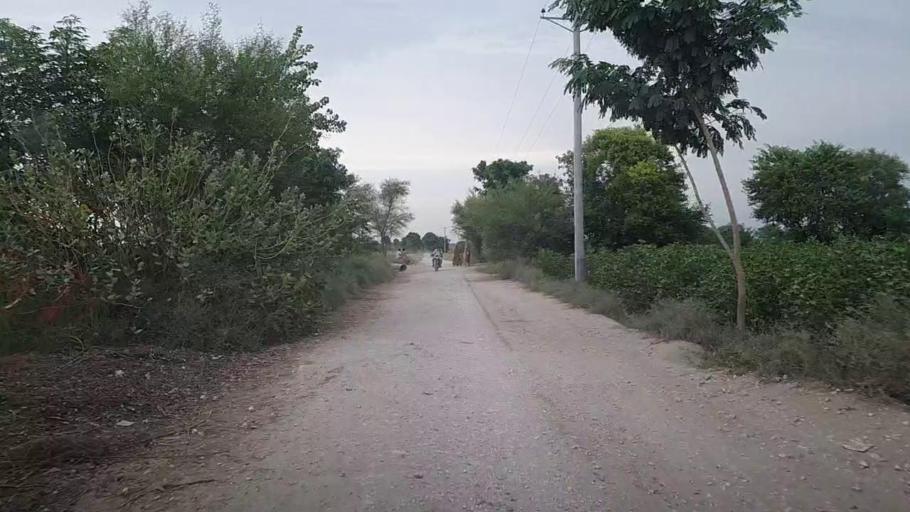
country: PK
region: Sindh
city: Karaundi
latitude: 26.9784
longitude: 68.3438
